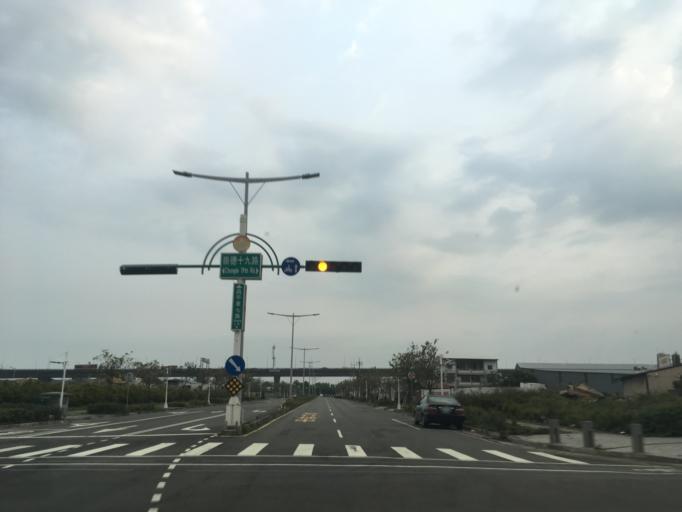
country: TW
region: Taiwan
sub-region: Taichung City
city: Taichung
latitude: 24.1977
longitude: 120.6934
